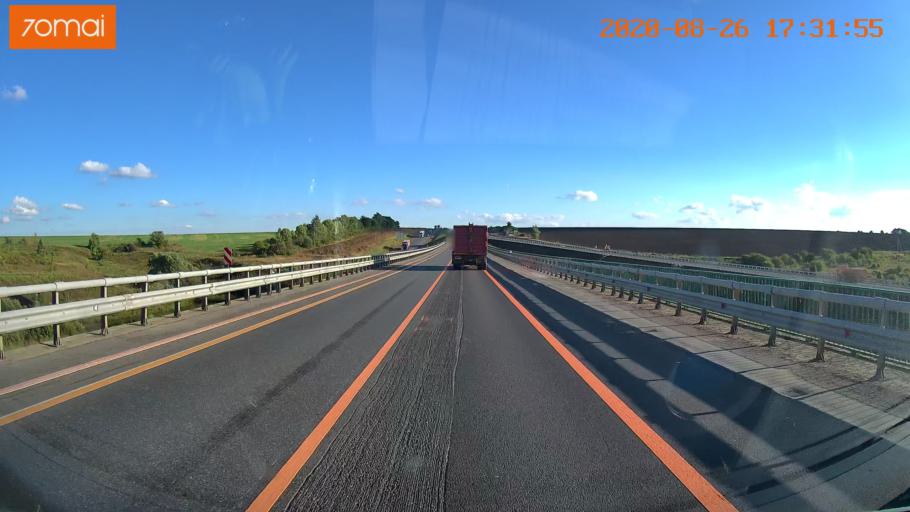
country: RU
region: Tula
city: Kazachka
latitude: 53.4285
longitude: 38.1797
